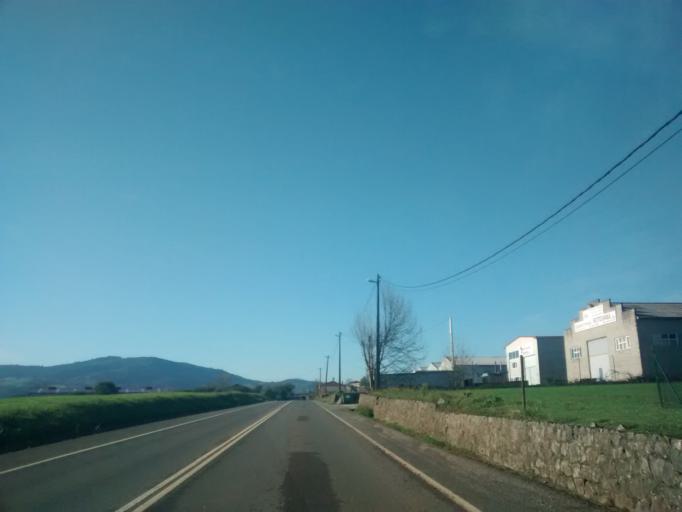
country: ES
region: Cantabria
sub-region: Provincia de Cantabria
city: Penagos
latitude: 43.3353
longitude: -3.8335
